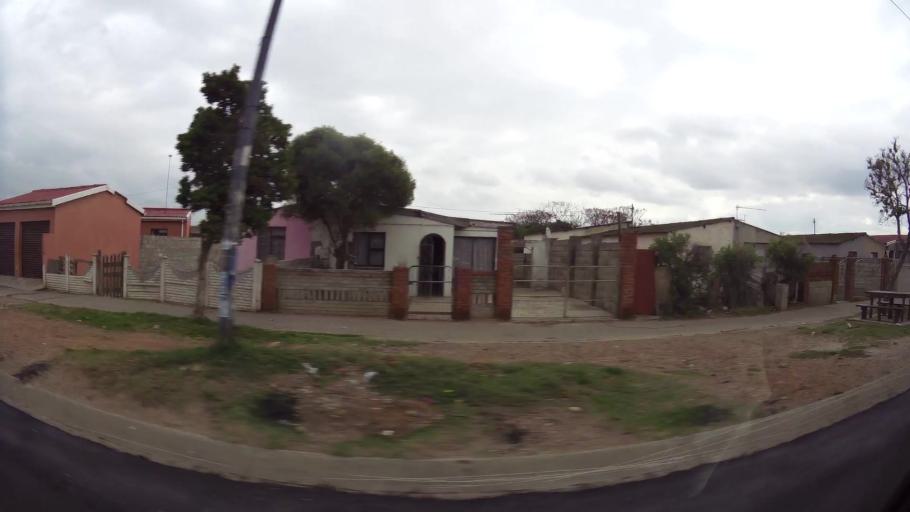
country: ZA
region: Eastern Cape
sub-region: Nelson Mandela Bay Metropolitan Municipality
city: Port Elizabeth
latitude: -33.8929
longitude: 25.5925
